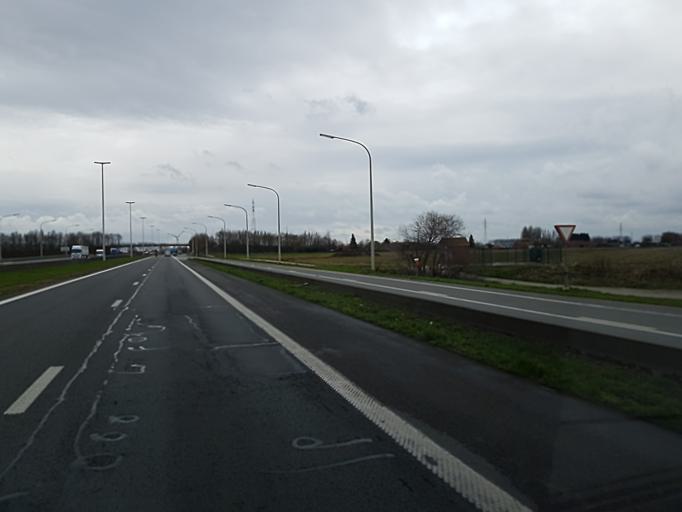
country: BE
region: Wallonia
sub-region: Province du Hainaut
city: Estaimpuis
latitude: 50.7156
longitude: 3.2972
